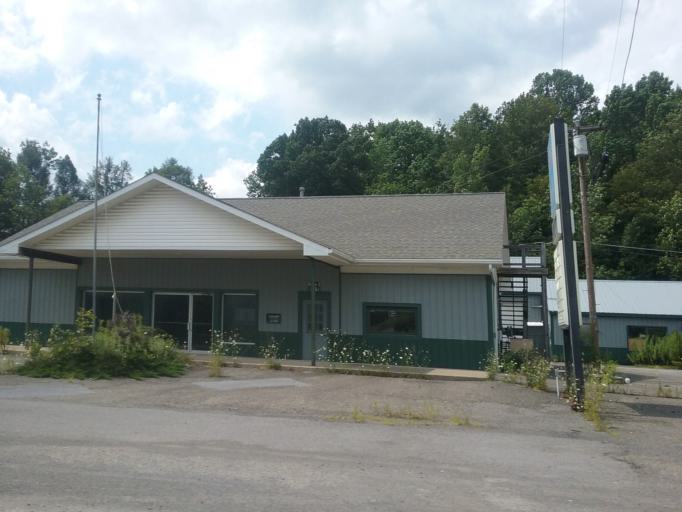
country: US
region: Pennsylvania
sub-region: Tioga County
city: Wellsboro
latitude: 41.7623
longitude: -77.2152
